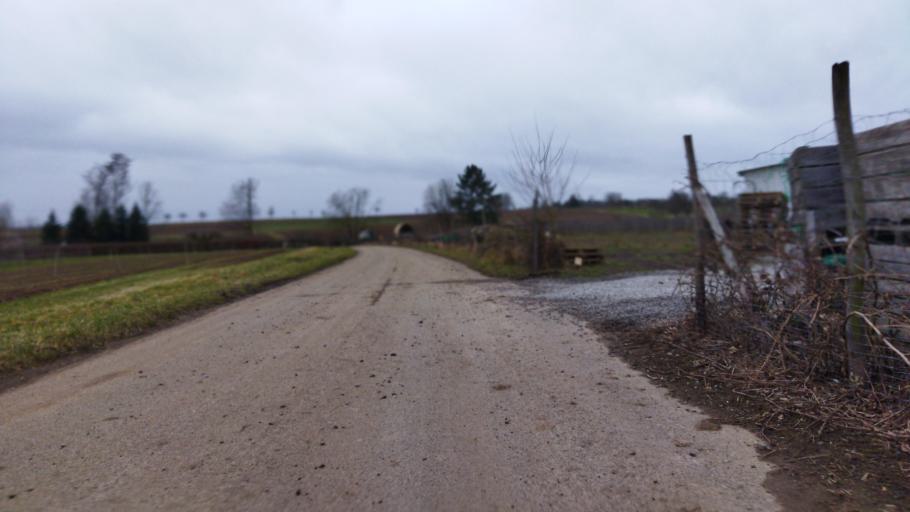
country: DE
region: Baden-Wuerttemberg
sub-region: Regierungsbezirk Stuttgart
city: Untergruppenbach
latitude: 49.0900
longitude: 9.2596
